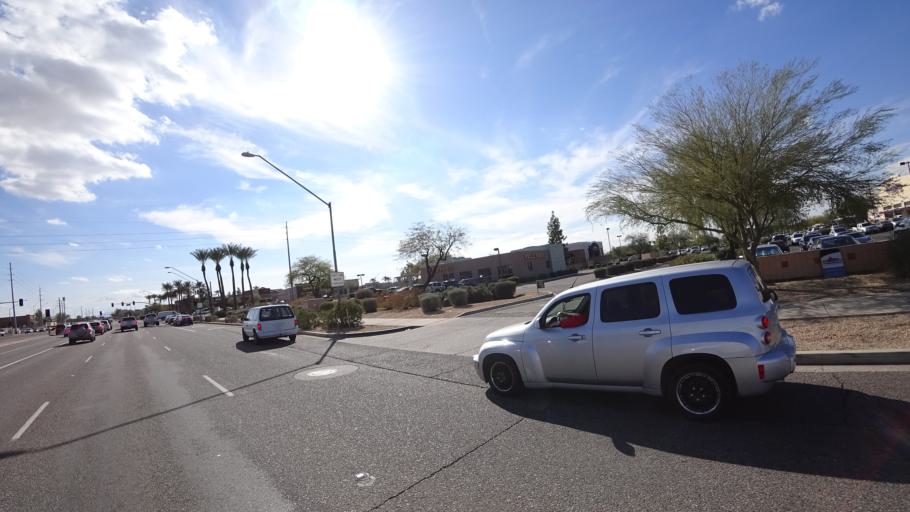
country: US
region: Arizona
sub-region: Maricopa County
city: Peoria
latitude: 33.6393
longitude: -112.2204
